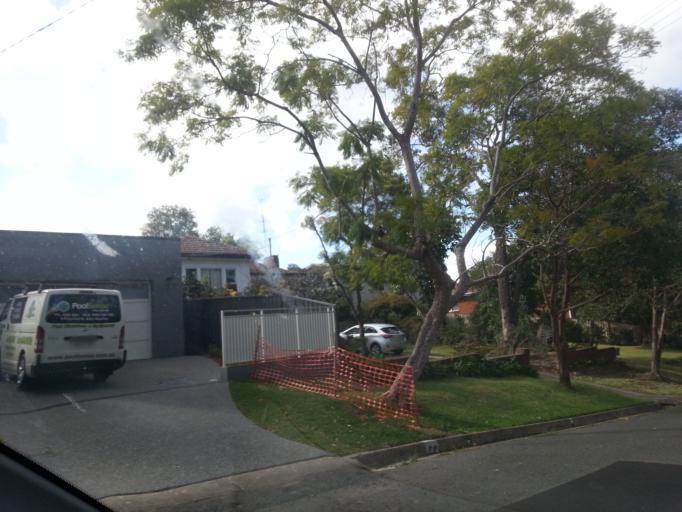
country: AU
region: New South Wales
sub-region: Wollongong
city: Keiraville
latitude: -34.4140
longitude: 150.8680
